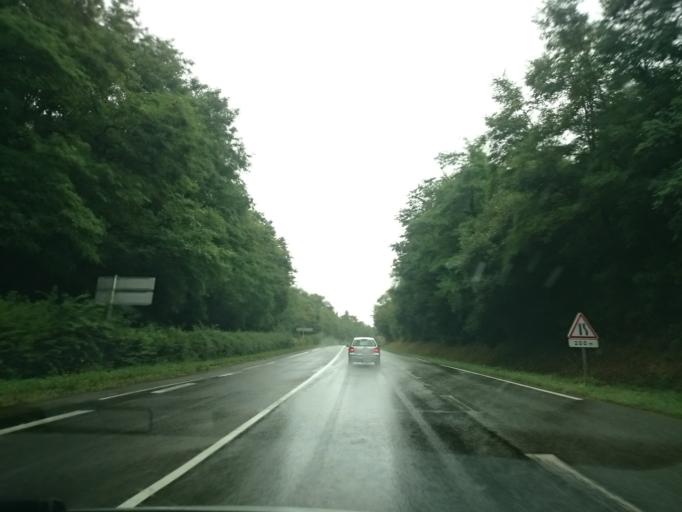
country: FR
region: Pays de la Loire
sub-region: Departement de la Loire-Atlantique
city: Orvault
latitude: 47.2452
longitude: -1.6353
